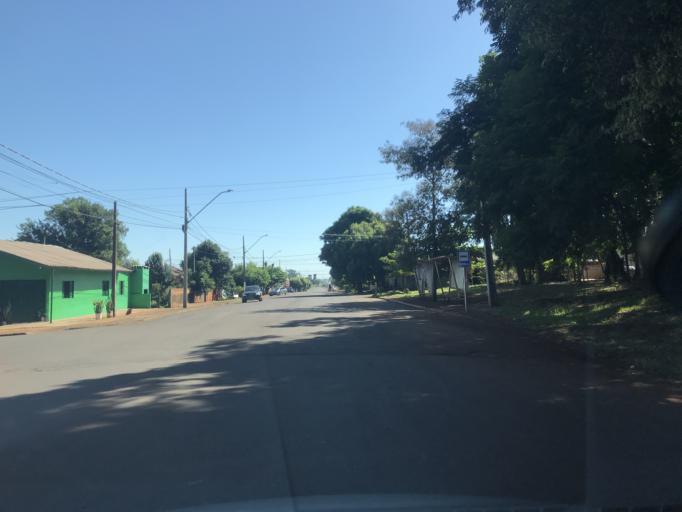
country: BR
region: Parana
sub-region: Palotina
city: Palotina
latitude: -24.2705
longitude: -53.8451
